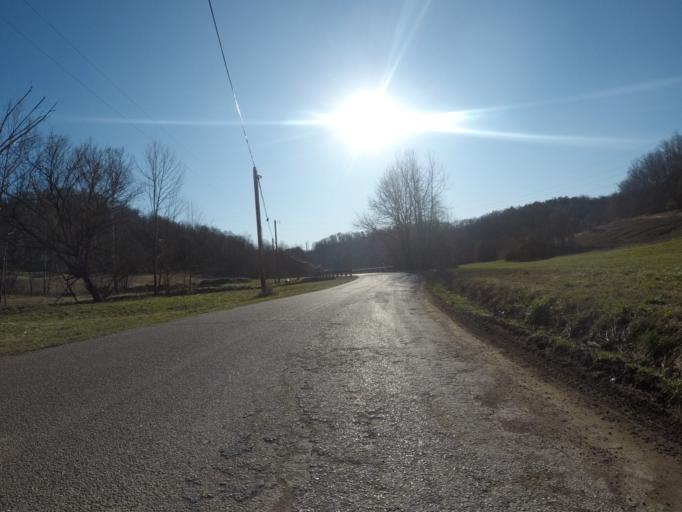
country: US
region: West Virginia
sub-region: Cabell County
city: Huntington
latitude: 38.5061
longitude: -82.4493
